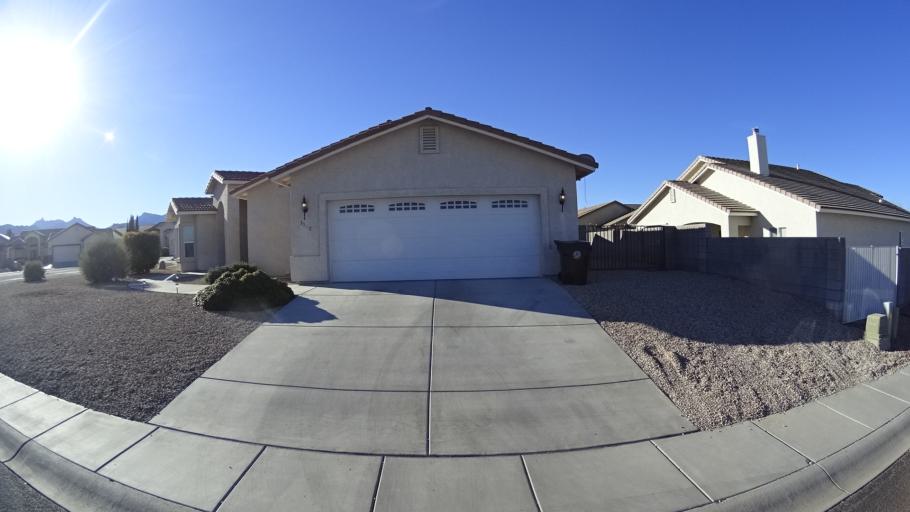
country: US
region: Arizona
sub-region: Mohave County
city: Kingman
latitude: 35.1951
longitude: -114.0054
